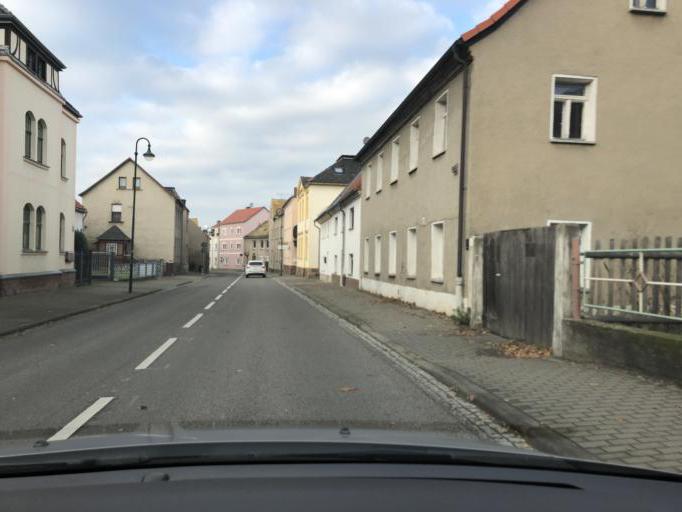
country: DE
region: Saxony
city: Nerchau
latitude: 51.2670
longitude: 12.7926
